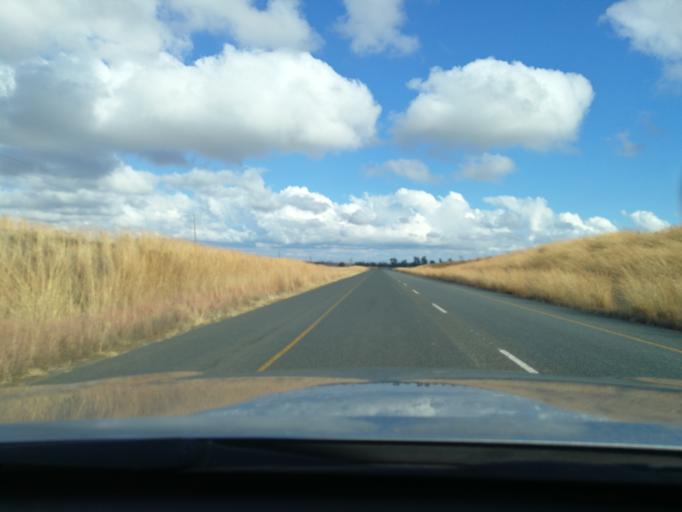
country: ZA
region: Orange Free State
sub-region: Thabo Mofutsanyana District Municipality
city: Reitz
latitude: -28.0054
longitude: 28.3772
